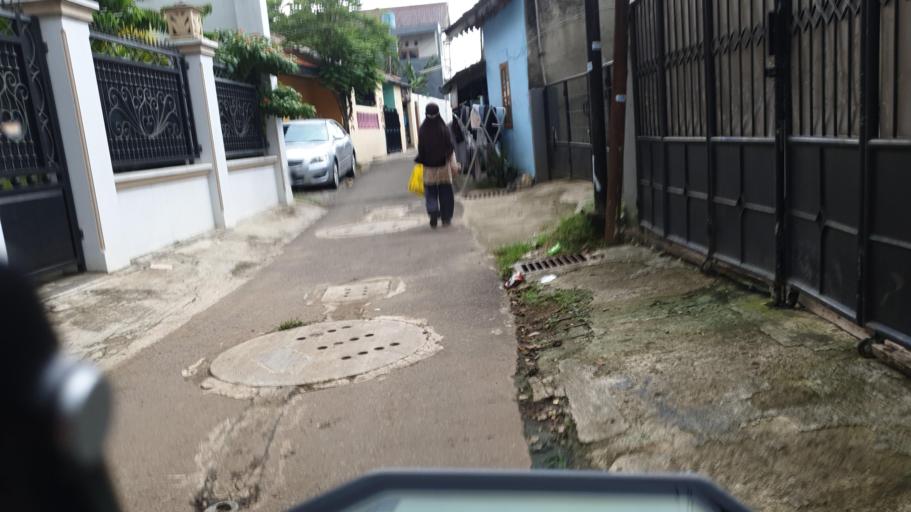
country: ID
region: West Java
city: Depok
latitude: -6.3411
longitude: 106.8220
